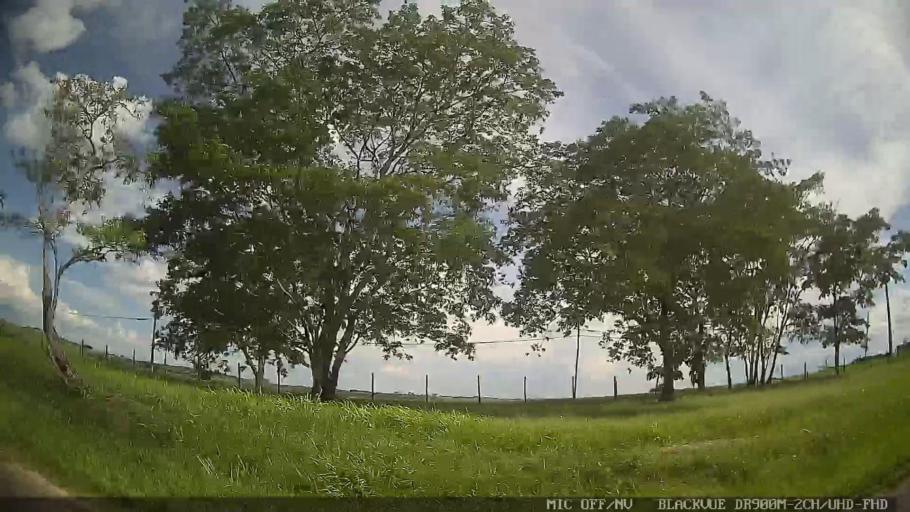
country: BR
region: Sao Paulo
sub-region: Conchas
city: Conchas
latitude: -23.0465
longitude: -47.9550
